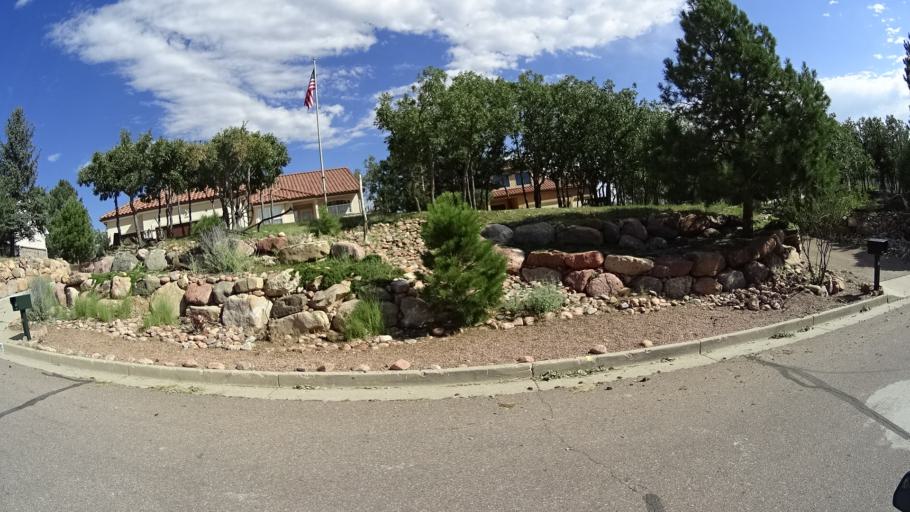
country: US
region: Colorado
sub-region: El Paso County
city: Fort Carson
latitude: 38.7651
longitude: -104.8297
